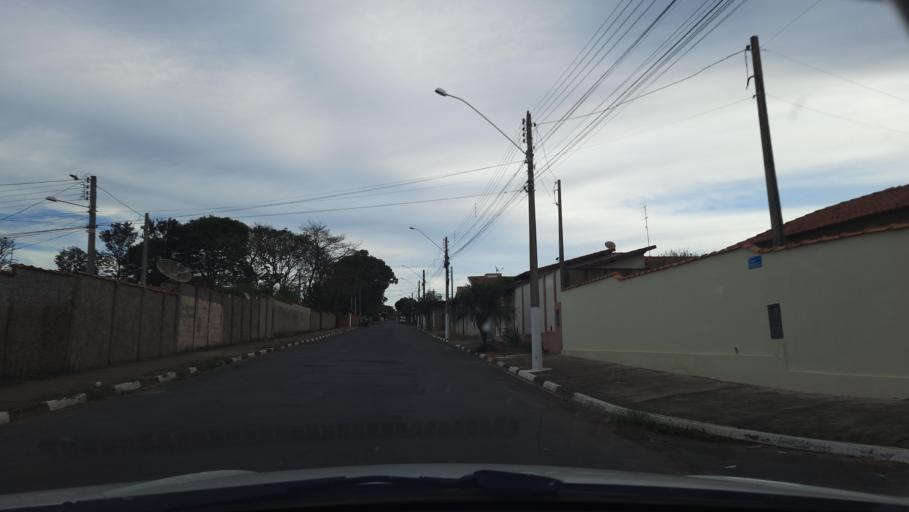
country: BR
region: Sao Paulo
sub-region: Casa Branca
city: Casa Branca
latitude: -21.7853
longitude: -47.0895
